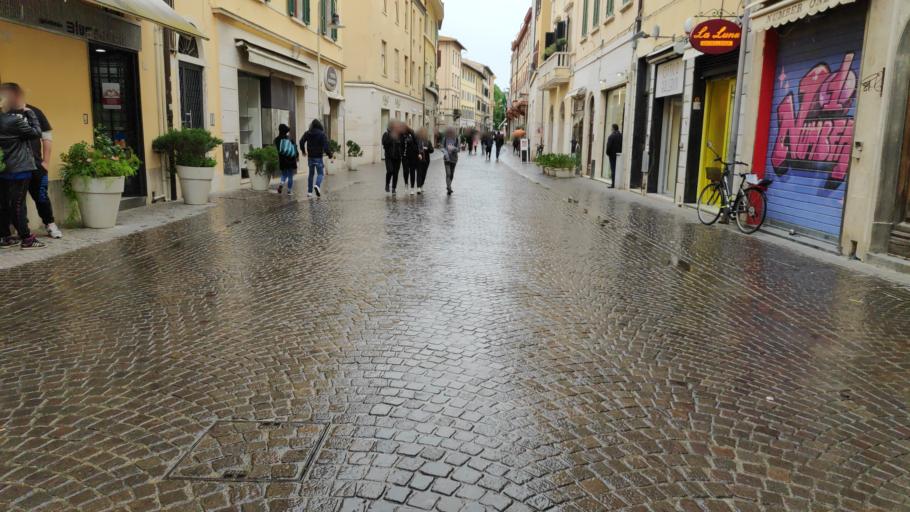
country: IT
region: Tuscany
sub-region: Provincia di Grosseto
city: Grosseto
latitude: 42.7606
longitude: 11.1133
